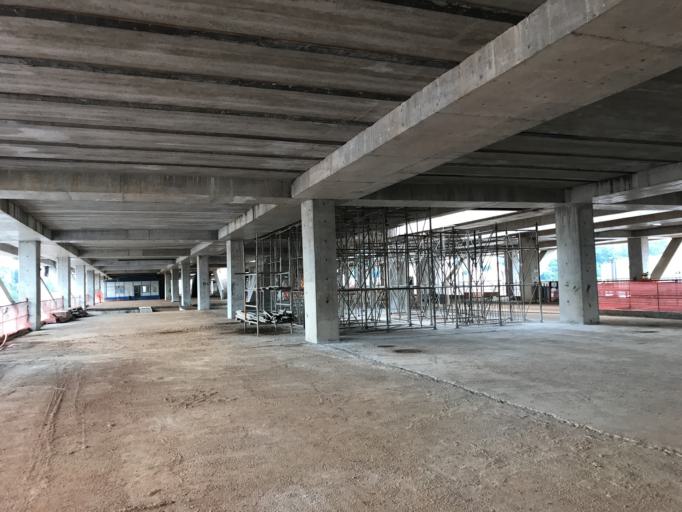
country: BR
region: Sao Paulo
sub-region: Taboao Da Serra
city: Taboao da Serra
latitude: -23.5918
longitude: -46.7358
